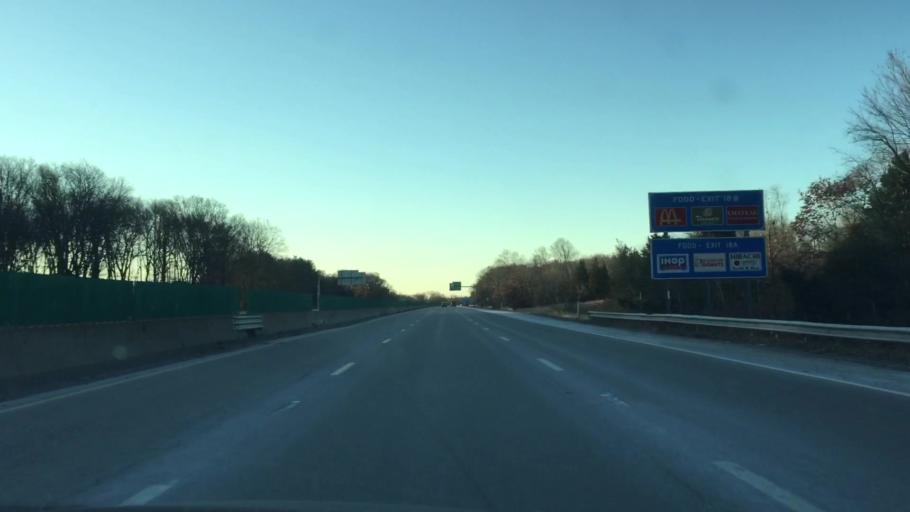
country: US
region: Massachusetts
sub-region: Norfolk County
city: Avon
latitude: 42.1089
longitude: -71.0589
